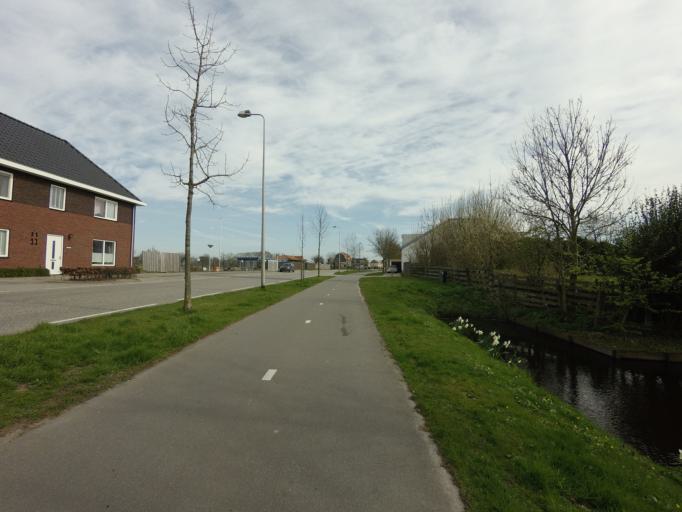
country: NL
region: South Holland
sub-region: Gemeente Alphen aan den Rijn
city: Alphen aan den Rijn
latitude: 52.1171
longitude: 4.6898
